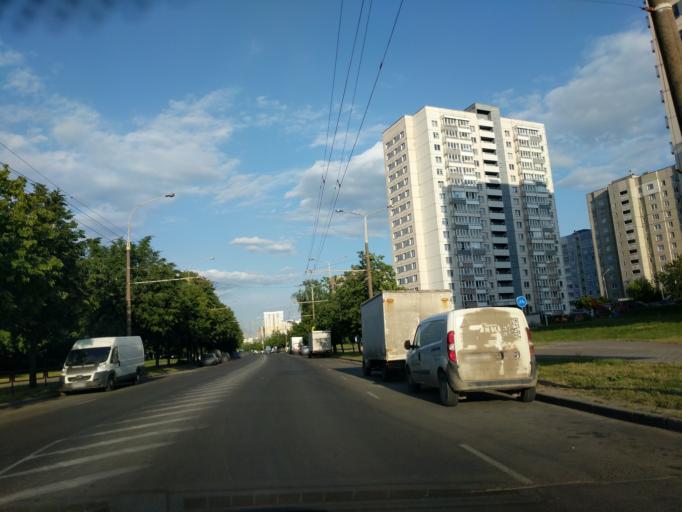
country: BY
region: Minsk
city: Malinovka
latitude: 53.8501
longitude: 27.4584
